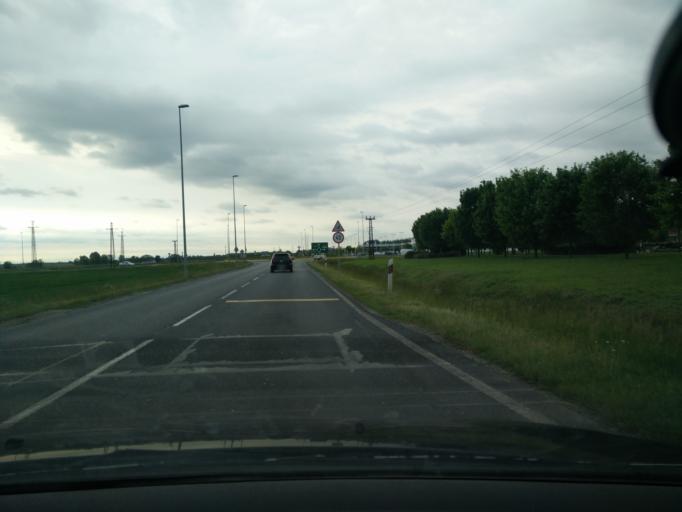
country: HU
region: Veszprem
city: Papa
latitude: 47.3205
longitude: 17.4478
